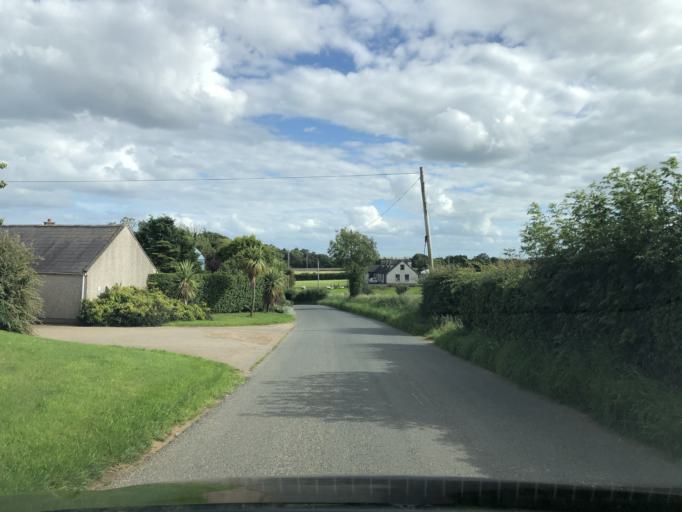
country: GB
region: Northern Ireland
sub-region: Ards District
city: Newtownards
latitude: 54.5621
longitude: -5.7099
